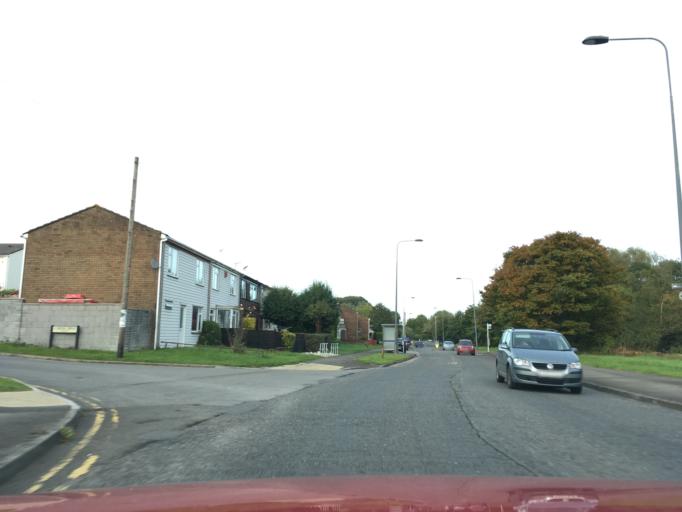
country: GB
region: England
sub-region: South Gloucestershire
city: Stoke Gifford
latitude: 51.5240
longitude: -2.5508
